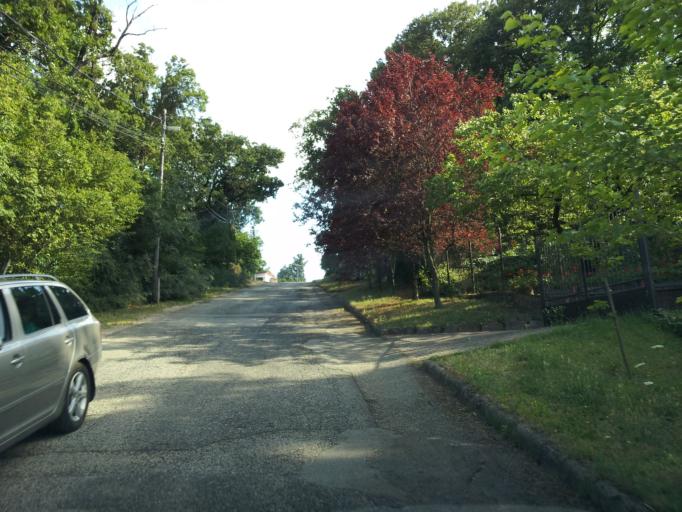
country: HU
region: Veszprem
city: Balatonalmadi
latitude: 47.0159
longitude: 18.0004
